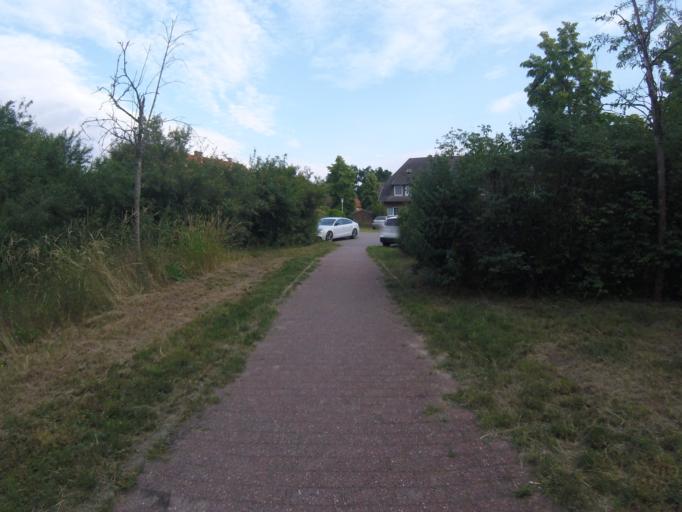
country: DE
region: Brandenburg
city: Konigs Wusterhausen
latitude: 52.2869
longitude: 13.6343
